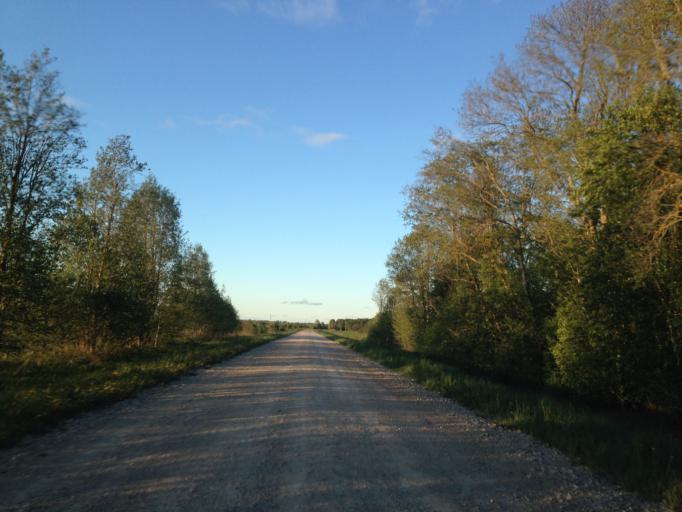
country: EE
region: Raplamaa
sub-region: Maerjamaa vald
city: Marjamaa
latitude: 58.7466
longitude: 24.1910
